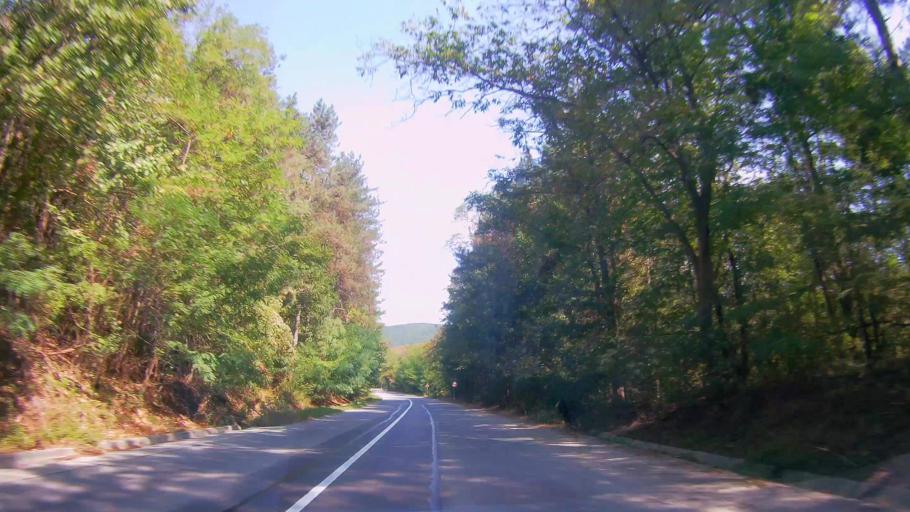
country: BG
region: Shumen
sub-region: Obshtina Smyadovo
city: Smyadovo
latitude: 43.0168
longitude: 27.0490
